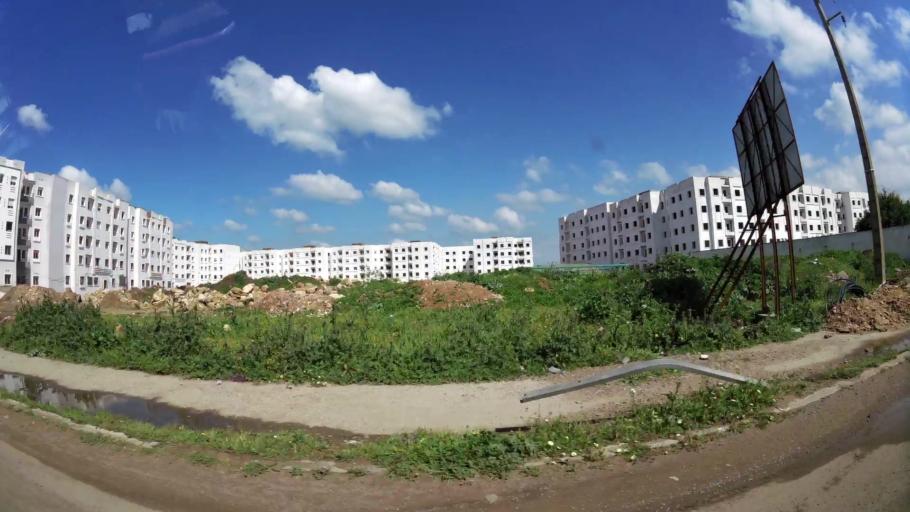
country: MA
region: Grand Casablanca
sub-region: Mediouna
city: Mediouna
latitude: 33.4427
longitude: -7.5201
